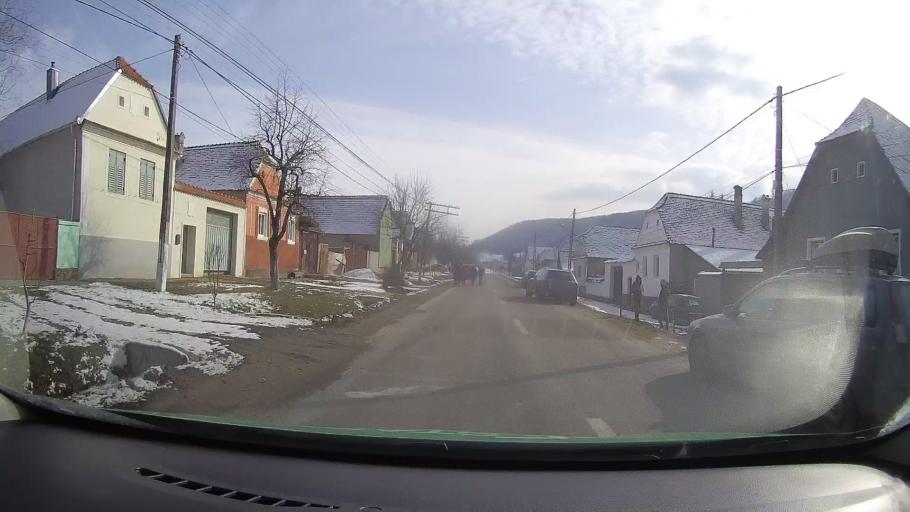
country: RO
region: Mures
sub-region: Comuna Apold
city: Saes
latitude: 46.1540
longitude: 24.7700
